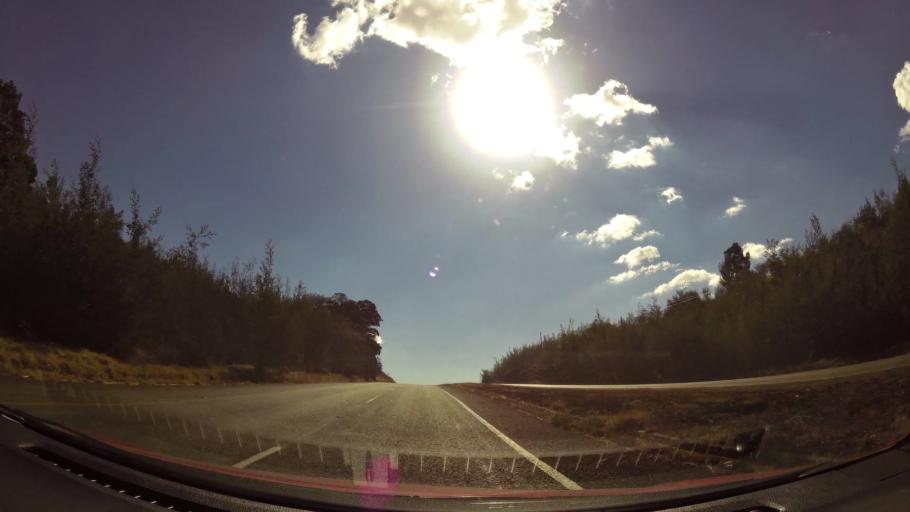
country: ZA
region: North-West
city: Fochville
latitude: -26.4243
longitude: 27.4623
